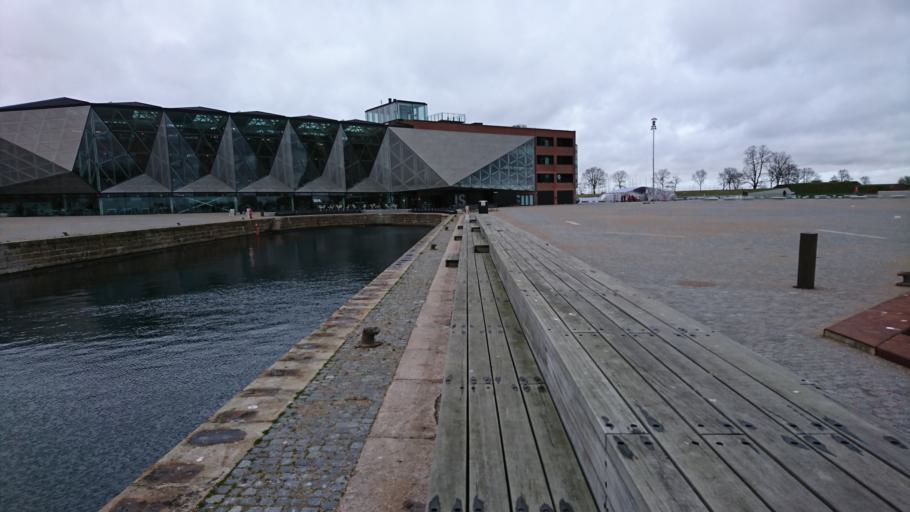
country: DK
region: Capital Region
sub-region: Helsingor Kommune
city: Helsingor
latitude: 56.0376
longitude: 12.6161
